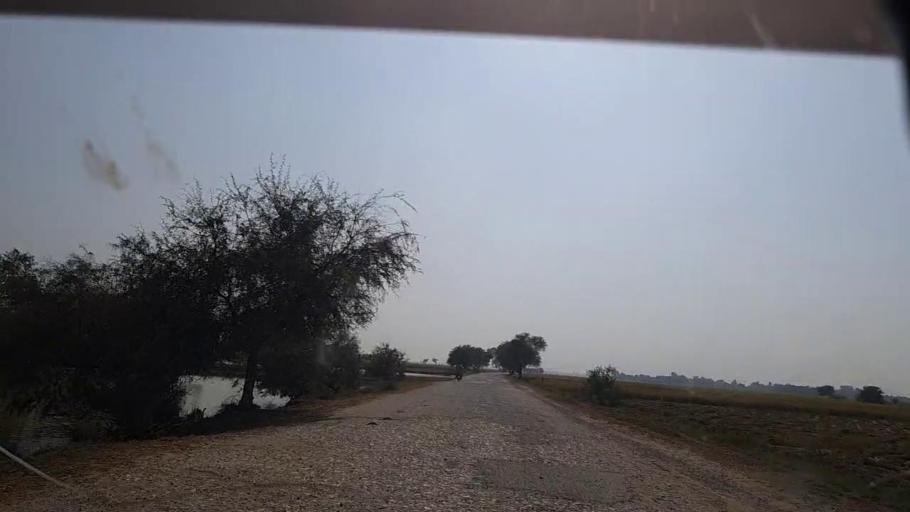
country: PK
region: Sindh
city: Shikarpur
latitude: 28.0966
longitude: 68.6105
